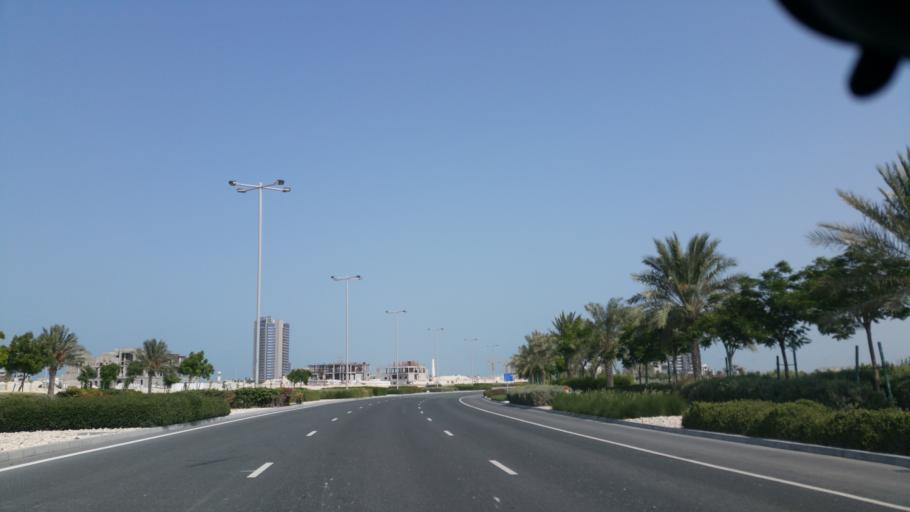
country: QA
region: Baladiyat Umm Salal
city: Umm Salal Muhammad
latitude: 25.4402
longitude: 51.5120
